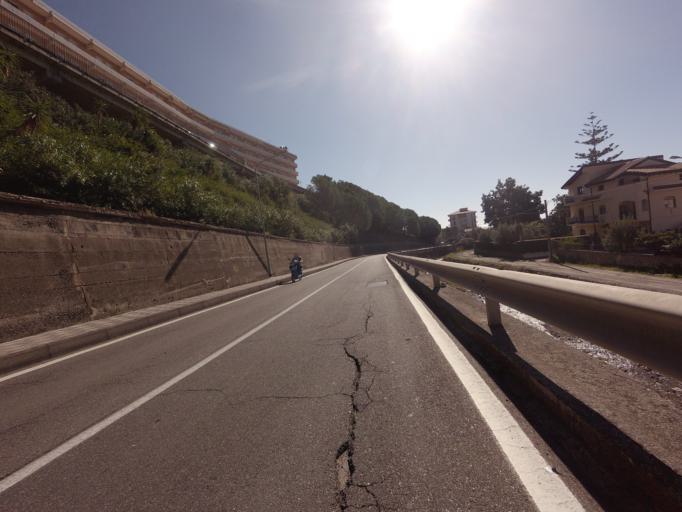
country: IT
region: Sicily
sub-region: Messina
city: Castelmola
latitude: 37.8455
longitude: 15.2783
